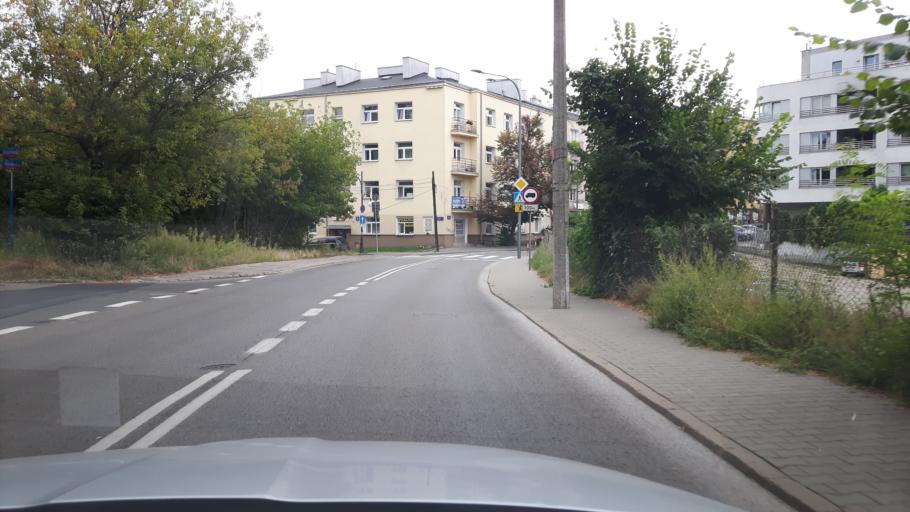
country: PL
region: Masovian Voivodeship
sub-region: Warszawa
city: Zoliborz
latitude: 52.2740
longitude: 20.9738
